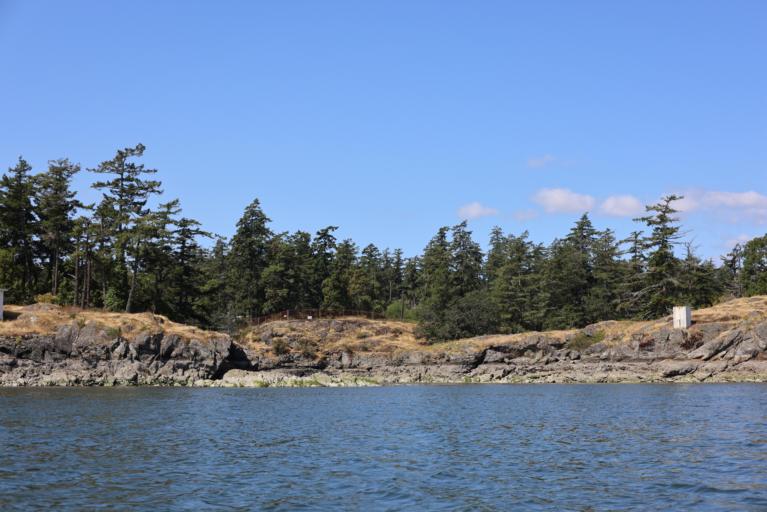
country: CA
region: British Columbia
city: Colwood
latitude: 48.4475
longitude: -123.4471
